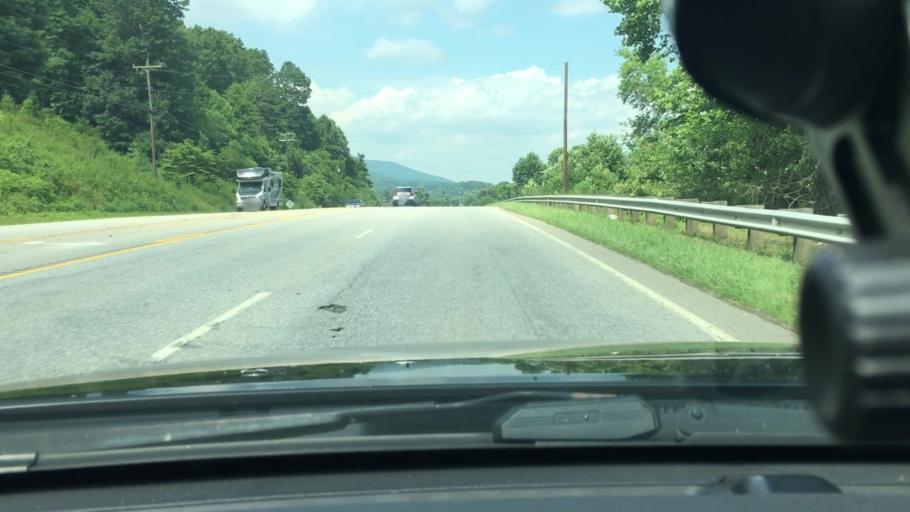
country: US
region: North Carolina
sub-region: Henderson County
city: Etowah
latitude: 35.3053
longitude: -82.6699
